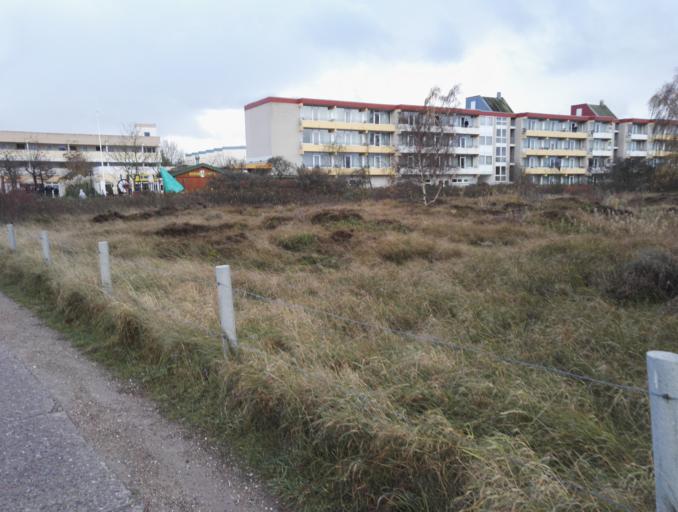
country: DE
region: Schleswig-Holstein
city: Wangels
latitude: 54.3113
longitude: 10.7959
